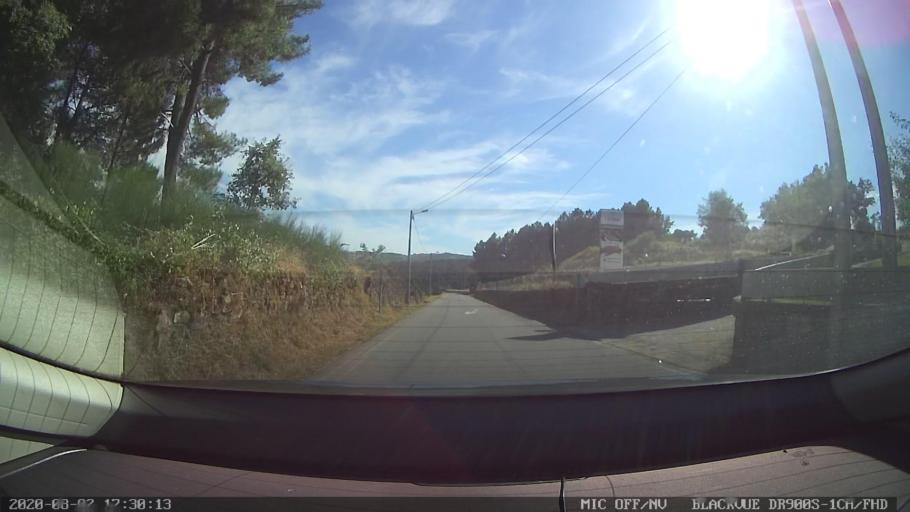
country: PT
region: Vila Real
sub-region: Sabrosa
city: Sabrosa
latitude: 41.3551
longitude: -7.5847
